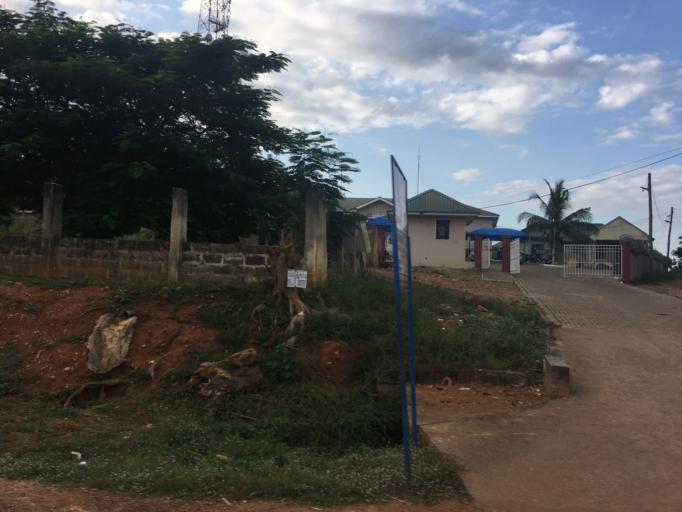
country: GH
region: Western
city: Bibiani
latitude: 6.4587
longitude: -2.3181
